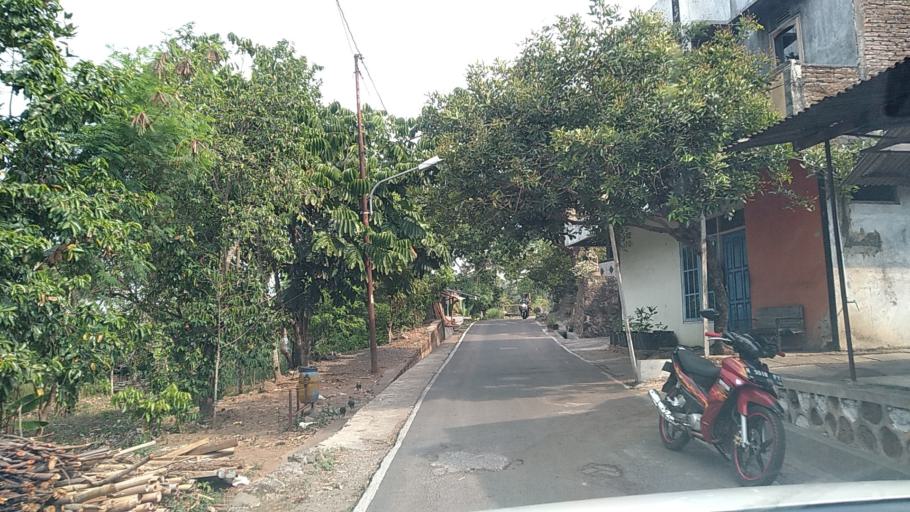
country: ID
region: Central Java
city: Ungaran
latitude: -7.1078
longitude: 110.3868
